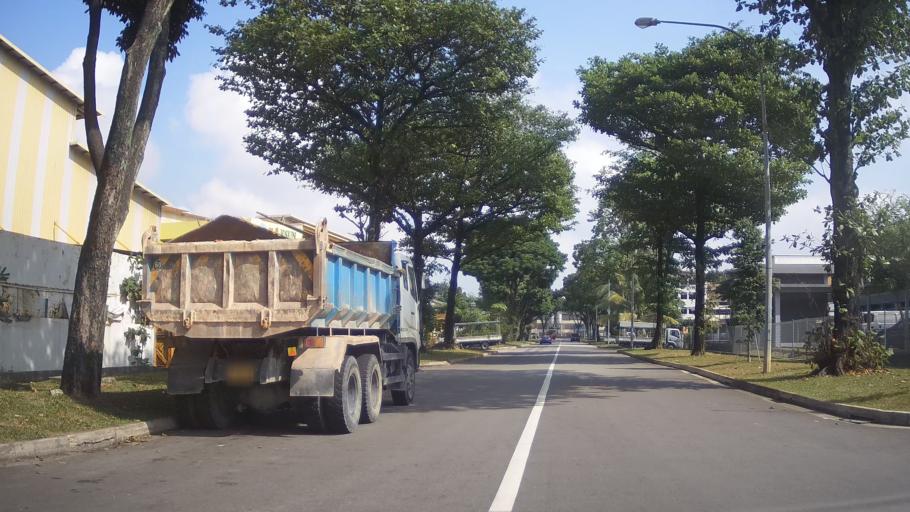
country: SG
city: Singapore
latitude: 1.3256
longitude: 103.7060
